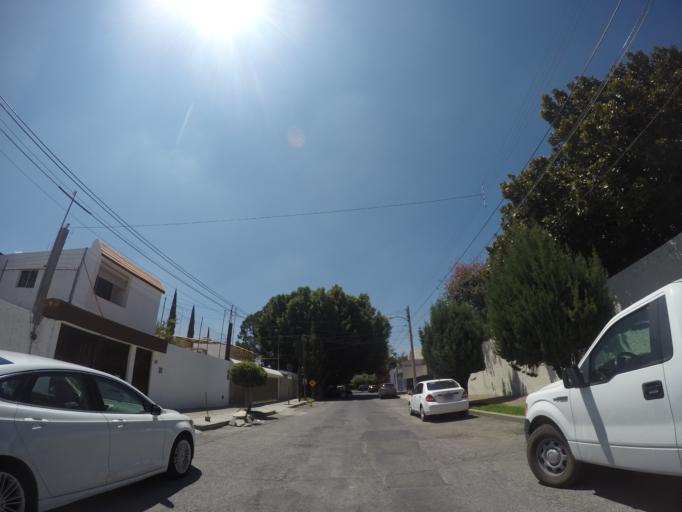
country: MX
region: San Luis Potosi
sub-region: San Luis Potosi
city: San Luis Potosi
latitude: 22.1484
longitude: -101.0054
